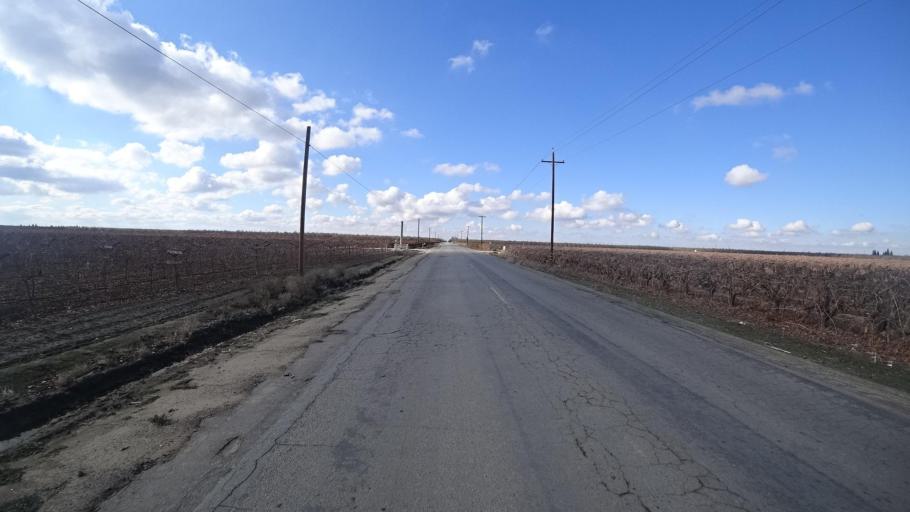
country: US
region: California
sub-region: Kern County
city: McFarland
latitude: 35.6888
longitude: -119.2535
